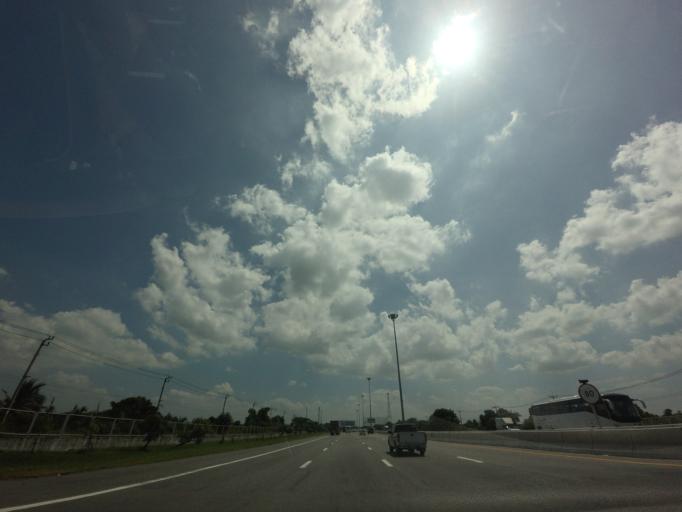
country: TH
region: Samut Prakan
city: Ban Khlong Bang Sao Thong
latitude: 13.6807
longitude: 100.8347
